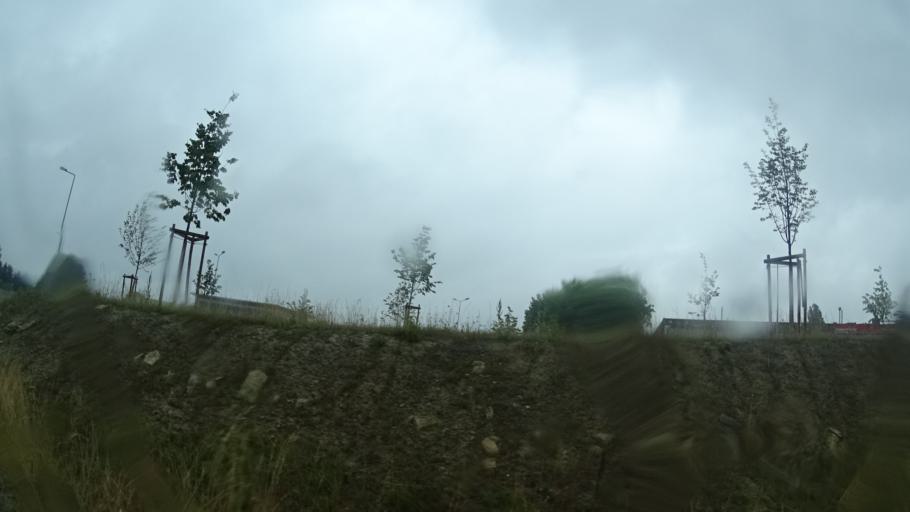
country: LU
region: Grevenmacher
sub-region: Canton de Remich
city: Mondorf-les-Bains
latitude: 49.5150
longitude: 6.3062
